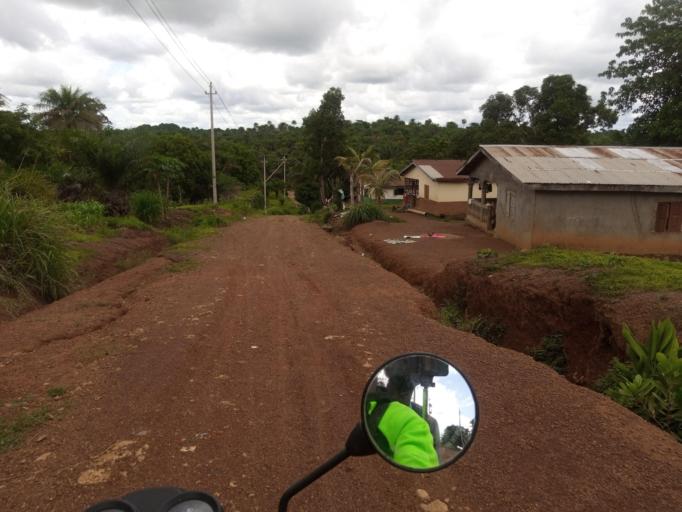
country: SL
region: Northern Province
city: Port Loko
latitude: 8.7608
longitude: -12.7771
